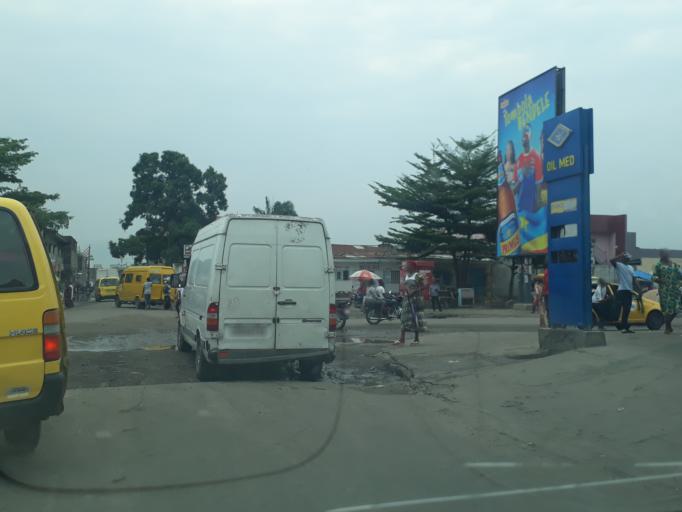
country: CD
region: Kinshasa
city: Kinshasa
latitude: -4.3198
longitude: 15.3206
